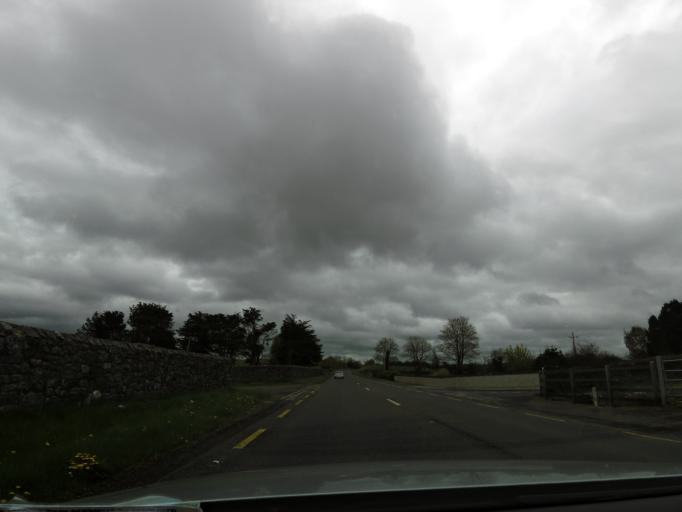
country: IE
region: Leinster
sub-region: Kilkenny
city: Ballyragget
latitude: 52.7175
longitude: -7.3374
